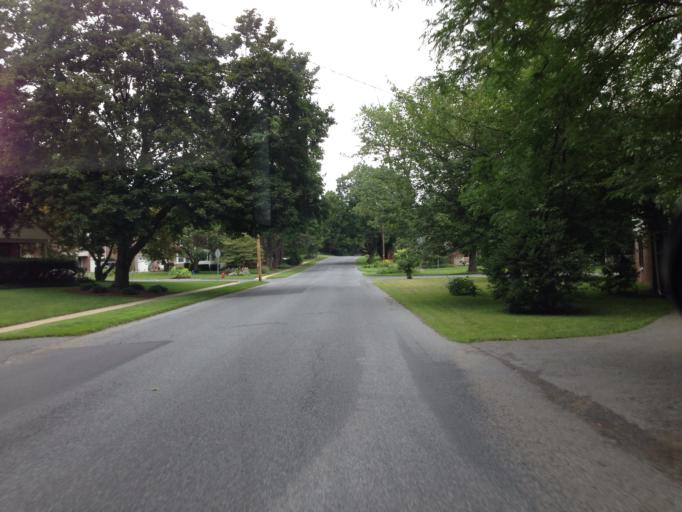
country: US
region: Pennsylvania
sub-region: Lancaster County
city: Lancaster
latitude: 40.0603
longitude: -76.2849
